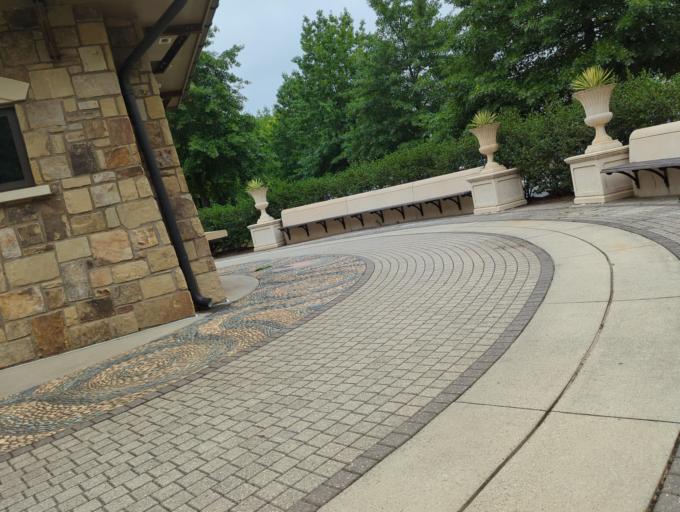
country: US
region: North Carolina
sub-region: Mecklenburg County
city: Charlotte
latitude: 35.2092
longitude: -80.8363
